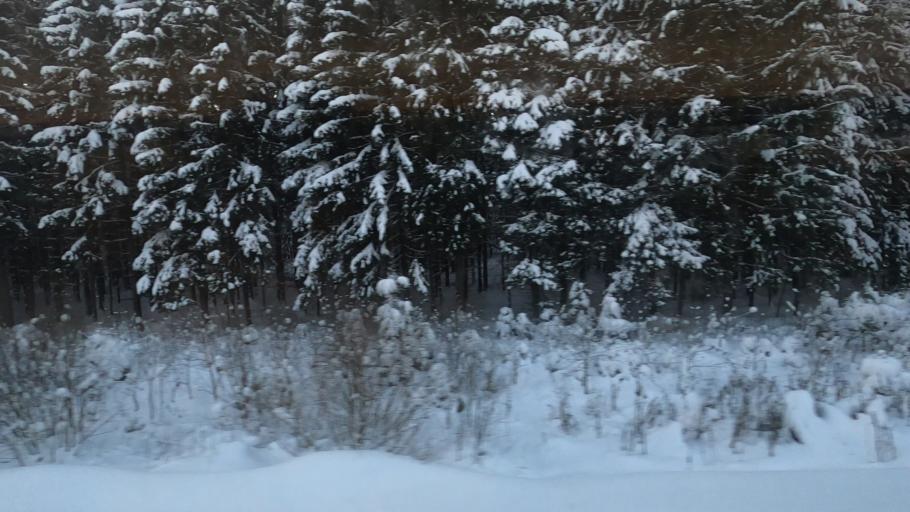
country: RU
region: Moskovskaya
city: Novo-Nikol'skoye
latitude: 56.6025
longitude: 37.5675
